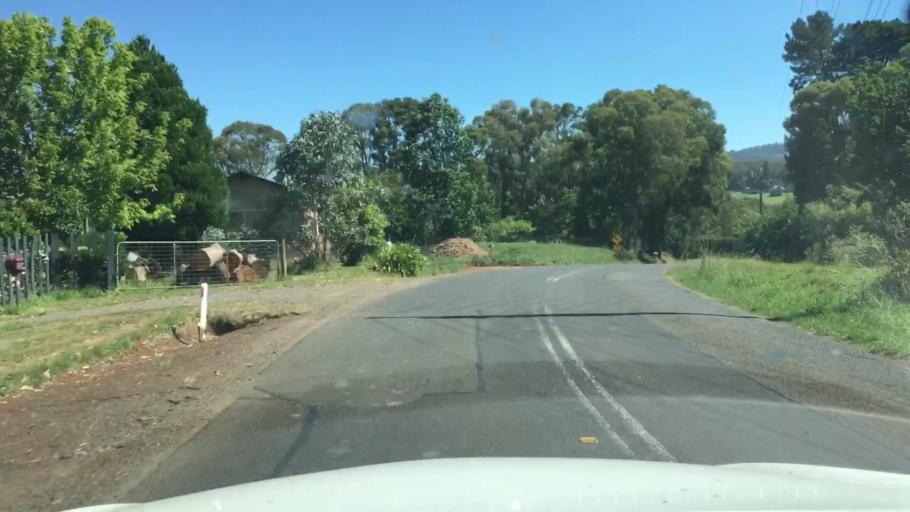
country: AU
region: Victoria
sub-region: Yarra Ranges
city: Mount Evelyn
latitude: -37.8145
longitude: 145.4233
